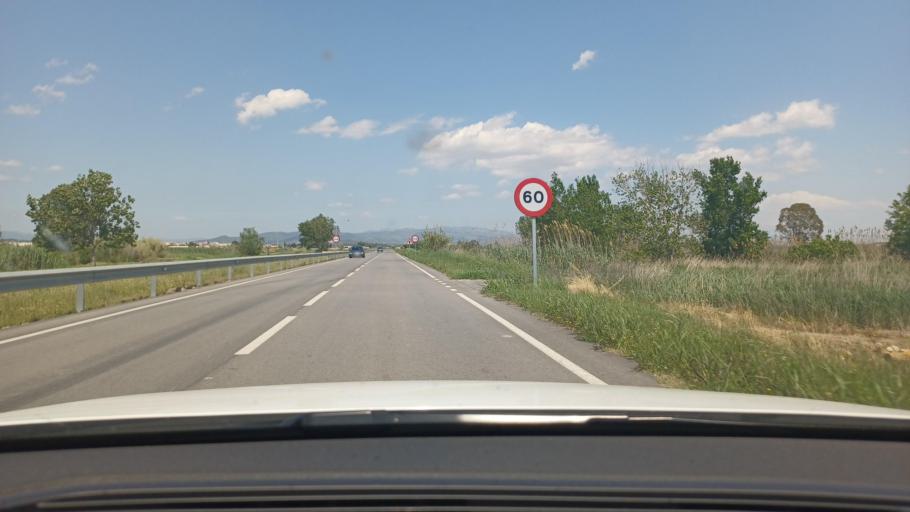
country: ES
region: Catalonia
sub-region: Provincia de Tarragona
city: Amposta
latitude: 40.6801
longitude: 0.5906
